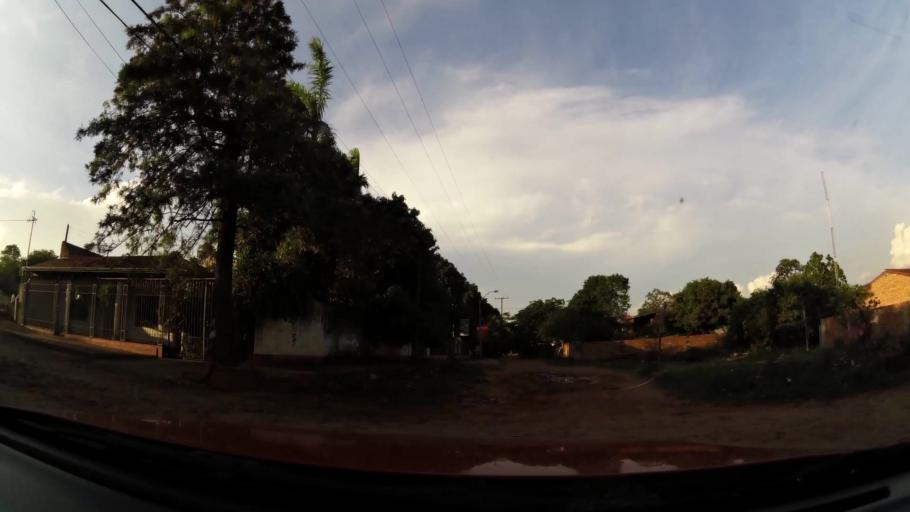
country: PY
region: Central
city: San Lorenzo
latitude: -25.3602
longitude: -57.5042
